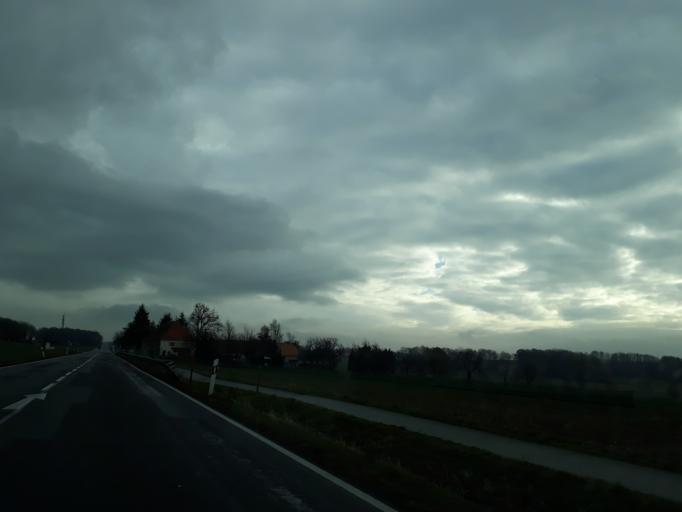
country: DE
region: Saxony
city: Hochkirch
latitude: 51.1352
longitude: 14.6030
